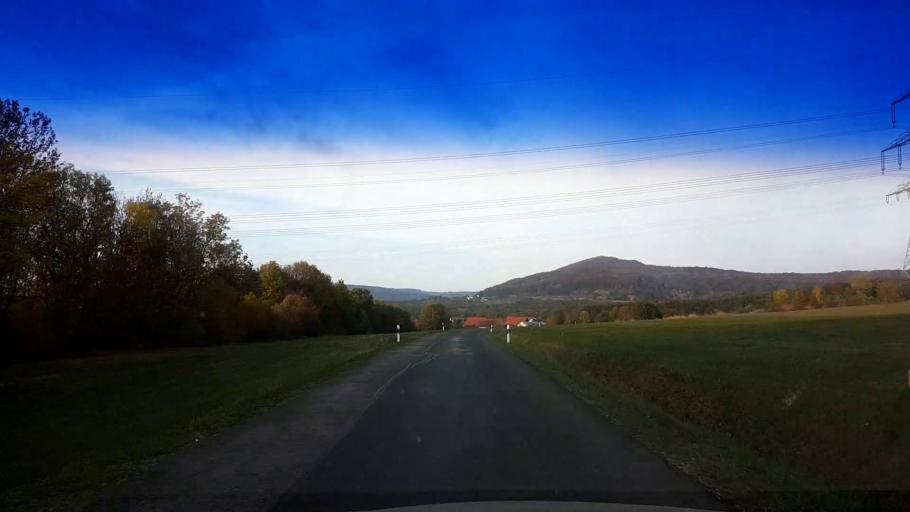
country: DE
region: Bavaria
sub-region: Upper Franconia
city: Schesslitz
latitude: 49.9653
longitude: 11.0585
